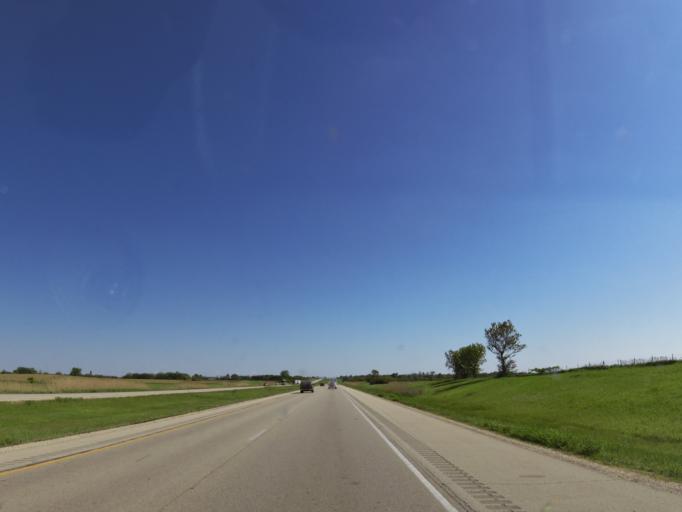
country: US
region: Illinois
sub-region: Ogle County
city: Rochelle
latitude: 41.8738
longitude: -89.0108
